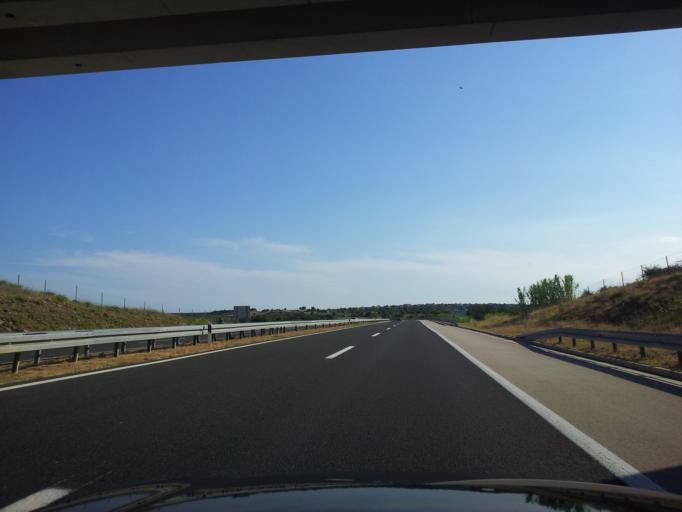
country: HR
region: Zadarska
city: Policnik
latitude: 44.1722
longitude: 15.4242
